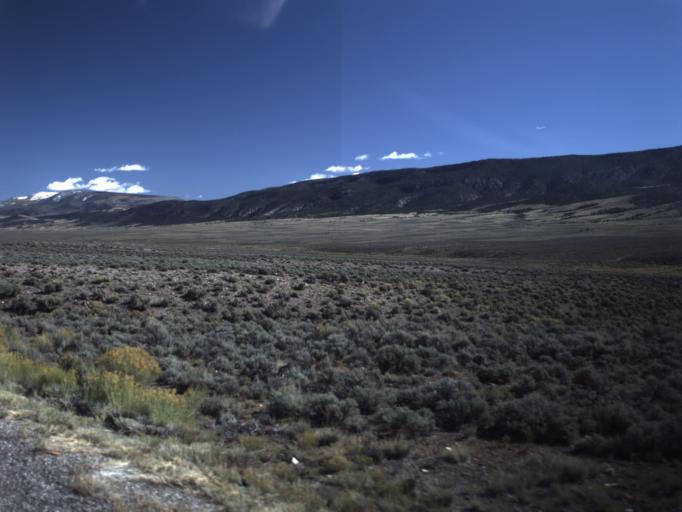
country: US
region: Utah
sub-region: Wayne County
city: Loa
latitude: 38.3653
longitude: -111.9407
